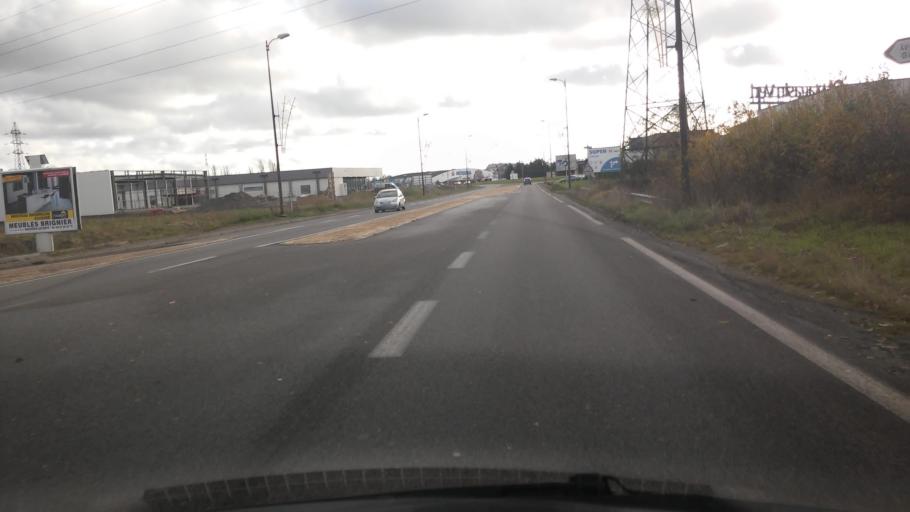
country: FR
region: Lorraine
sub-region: Departement de la Moselle
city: Talange
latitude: 49.2428
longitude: 6.1728
